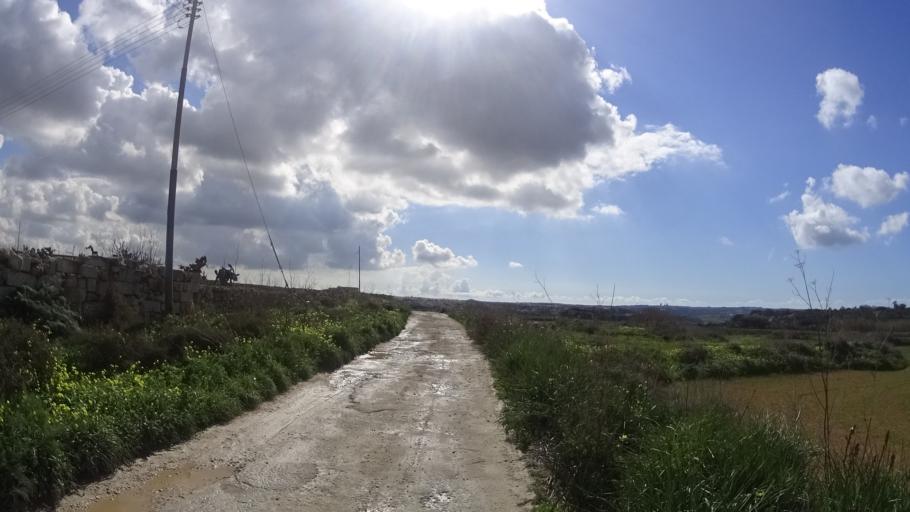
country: MT
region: L-Imtarfa
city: Imtarfa
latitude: 35.9039
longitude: 14.3847
